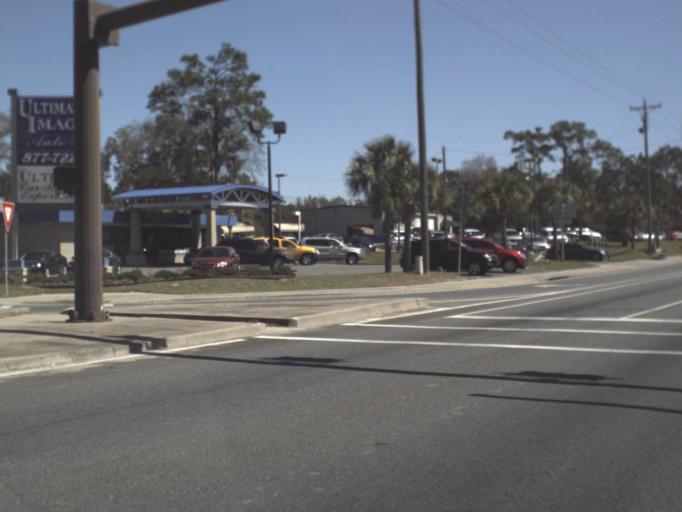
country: US
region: Florida
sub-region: Leon County
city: Tallahassee
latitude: 30.3759
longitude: -84.2925
